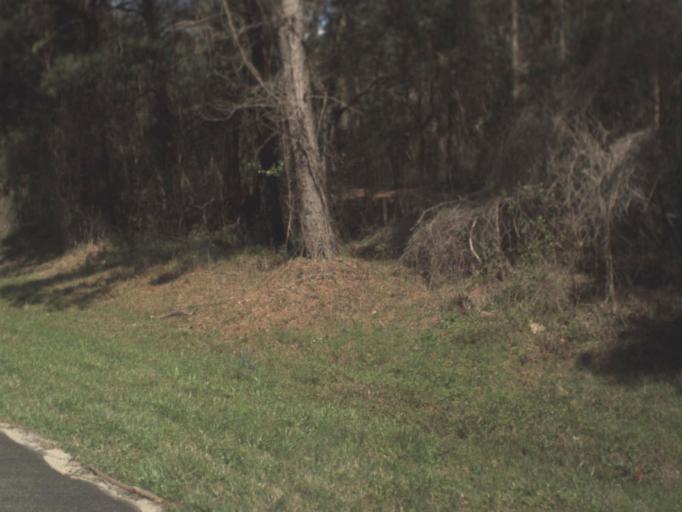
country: US
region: Florida
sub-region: Gadsden County
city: Quincy
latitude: 30.5890
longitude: -84.5004
